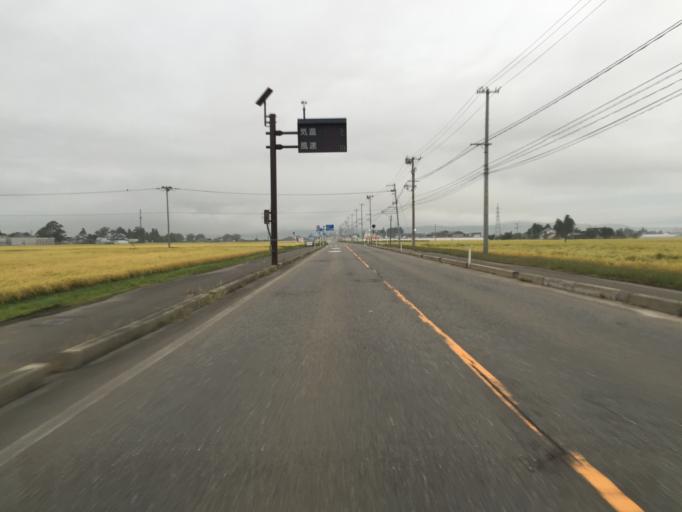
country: JP
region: Fukushima
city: Kitakata
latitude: 37.5548
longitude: 139.8704
